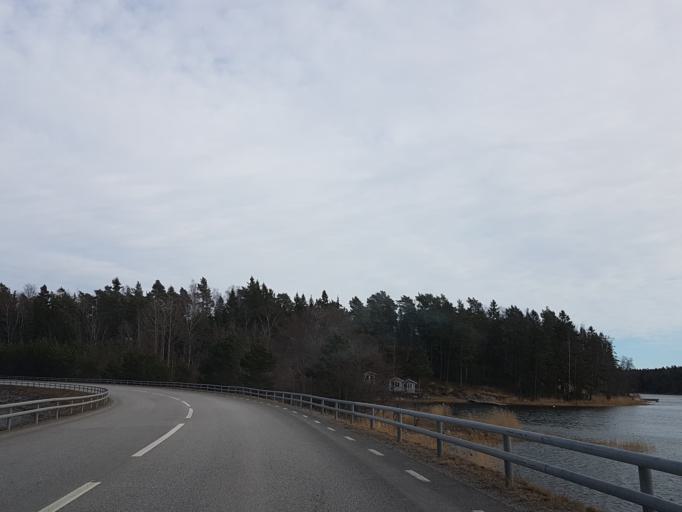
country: SE
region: Stockholm
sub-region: Norrtalje Kommun
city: Norrtalje
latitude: 59.6802
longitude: 18.8084
